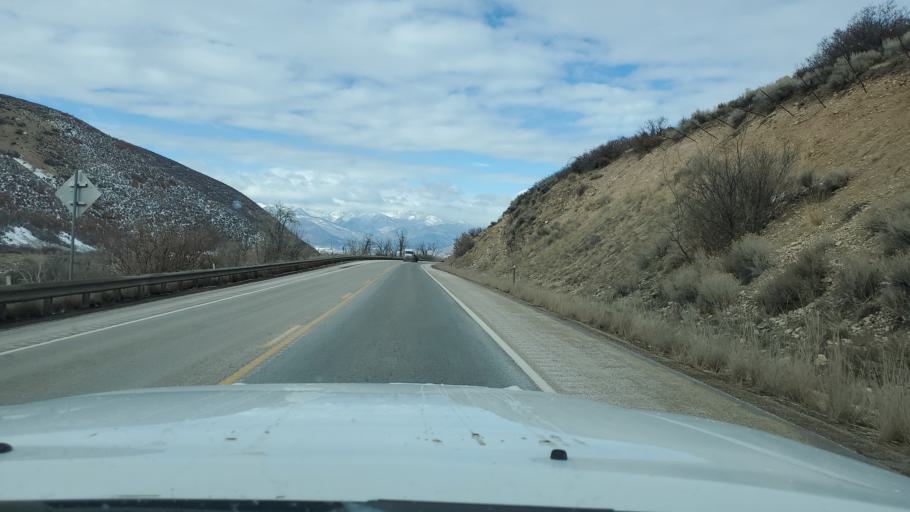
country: US
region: Utah
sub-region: Wasatch County
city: Heber
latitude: 40.4454
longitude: -111.3646
